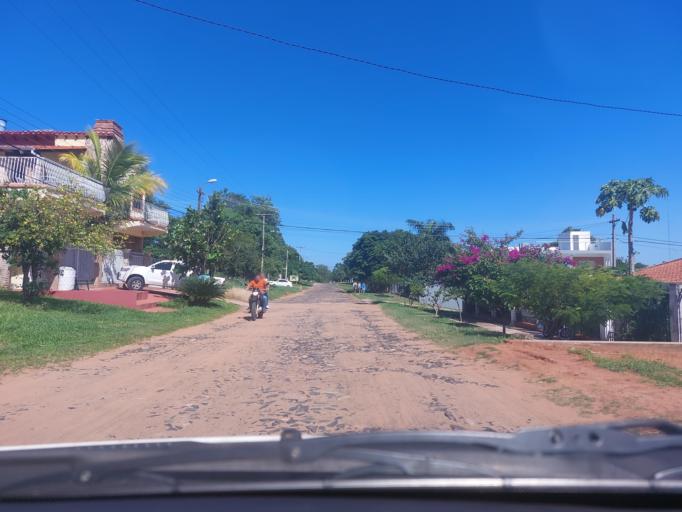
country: PY
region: San Pedro
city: Guayaybi
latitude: -24.6771
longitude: -56.4474
